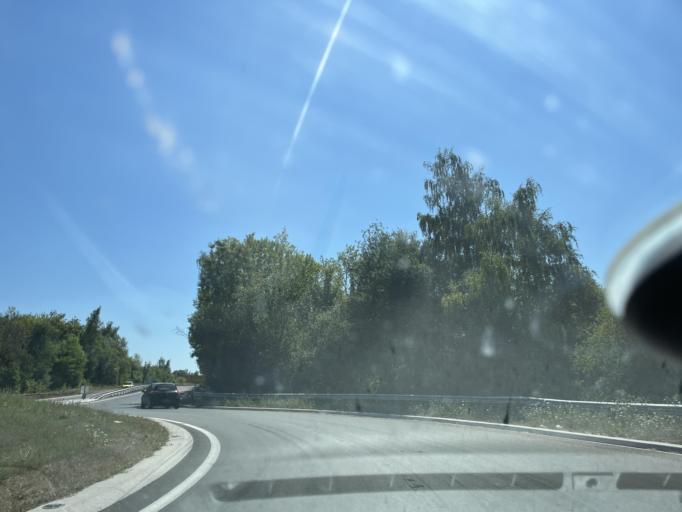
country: FR
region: Haute-Normandie
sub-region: Departement de la Seine-Maritime
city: Lillebonne
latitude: 49.5059
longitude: 0.5352
